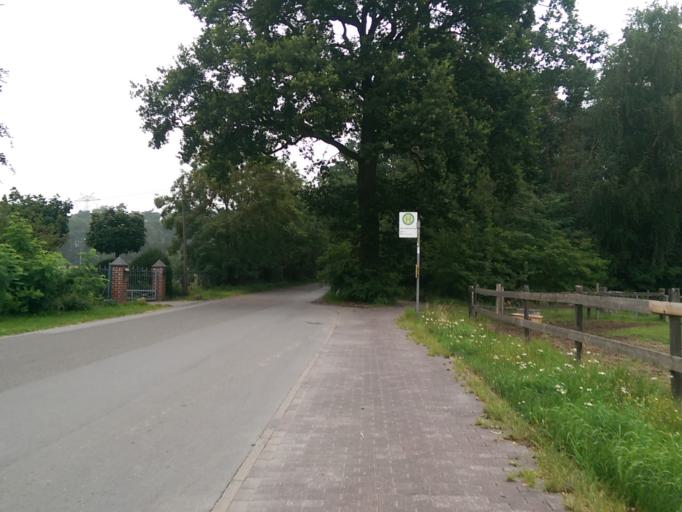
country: DE
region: North Rhine-Westphalia
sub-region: Regierungsbezirk Detmold
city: Guetersloh
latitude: 51.9041
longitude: 8.3306
